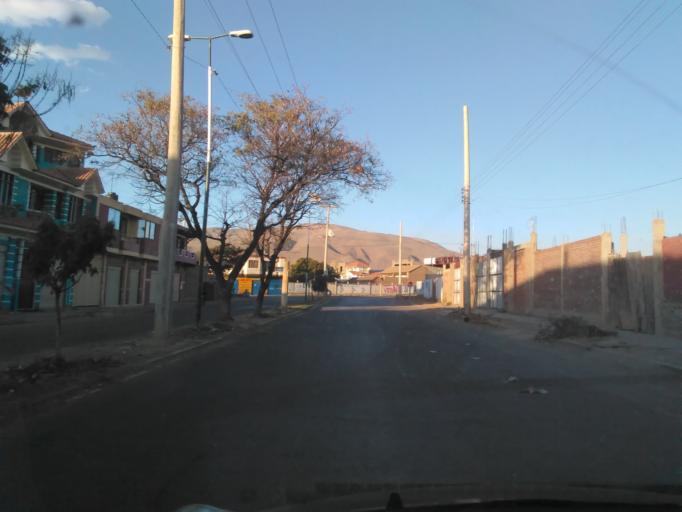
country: BO
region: Cochabamba
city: Punata
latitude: -17.5428
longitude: -65.8308
